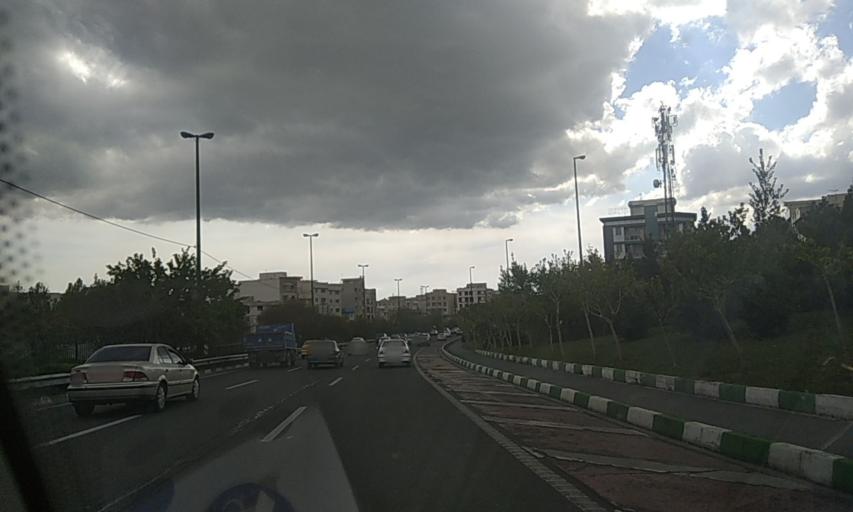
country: IR
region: Tehran
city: Tajrish
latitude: 35.7699
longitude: 51.3339
